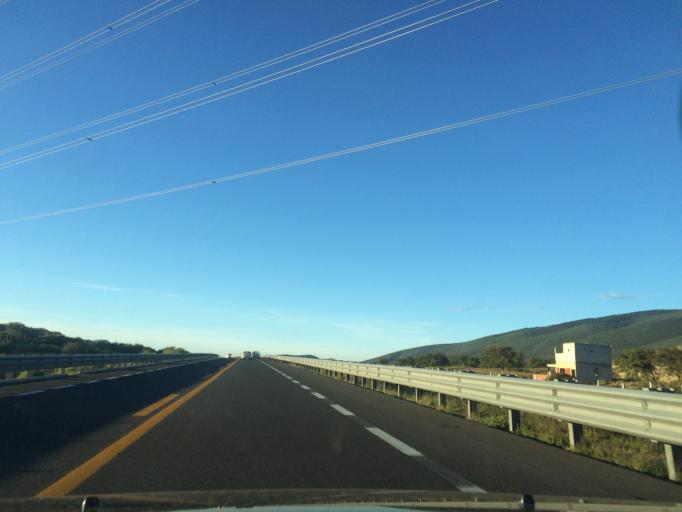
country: MX
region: Puebla
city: Morelos Canada
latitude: 18.7027
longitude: -97.4665
